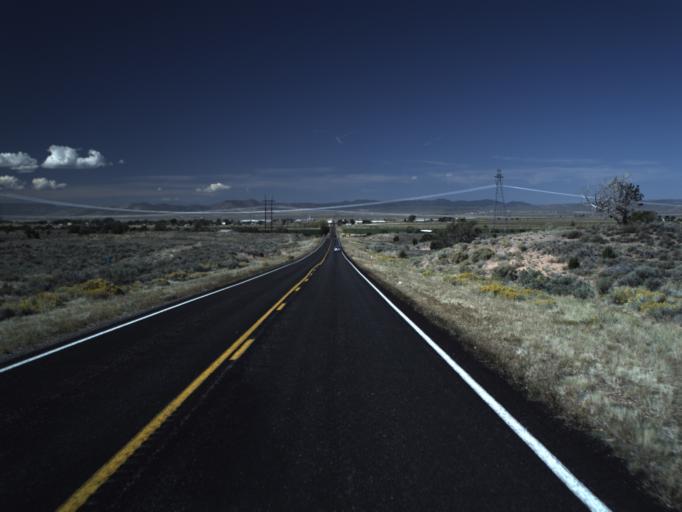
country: US
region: Utah
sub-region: Washington County
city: Enterprise
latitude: 37.6749
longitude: -113.5221
